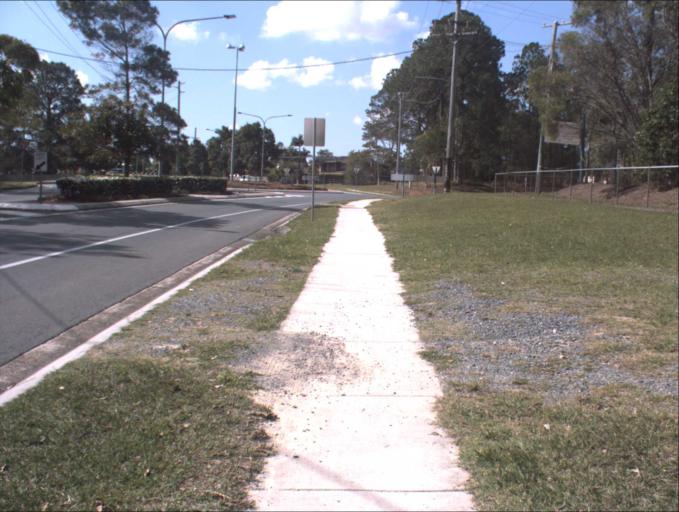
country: AU
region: Queensland
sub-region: Logan
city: Park Ridge South
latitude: -27.6977
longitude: 153.0124
